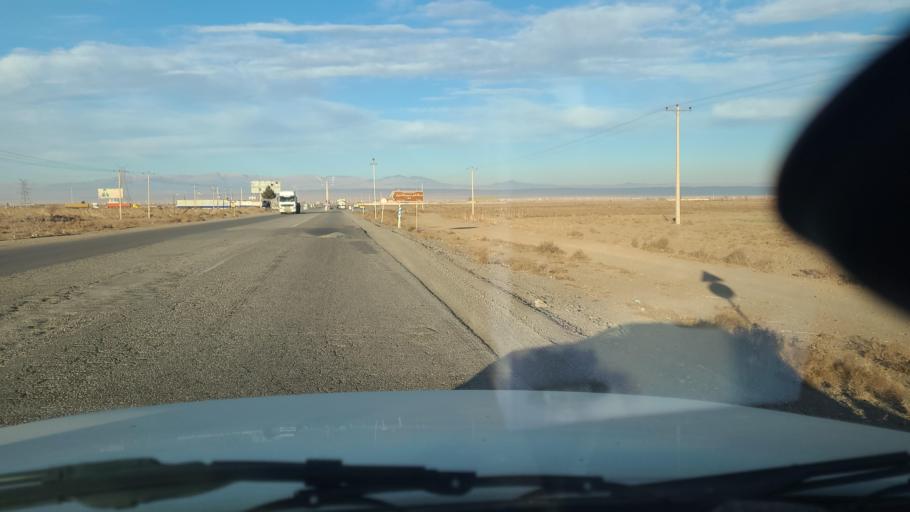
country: IR
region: Razavi Khorasan
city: Neqab
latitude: 36.5824
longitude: 57.5802
